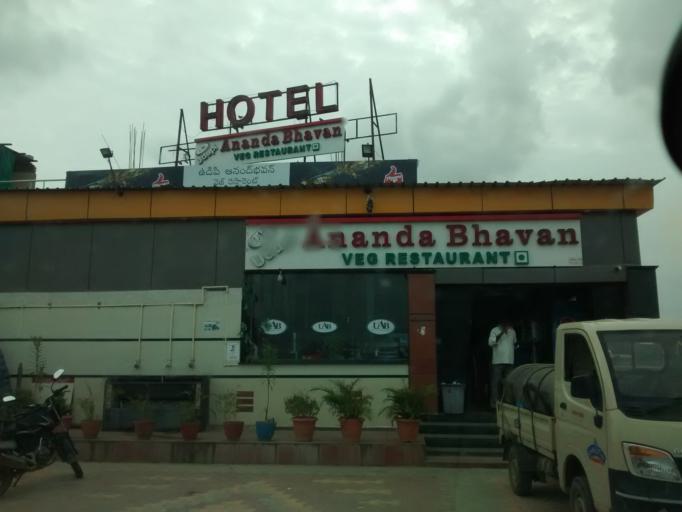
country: IN
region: Telangana
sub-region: Mahbubnagar
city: Wanparti
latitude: 16.2137
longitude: 77.9828
